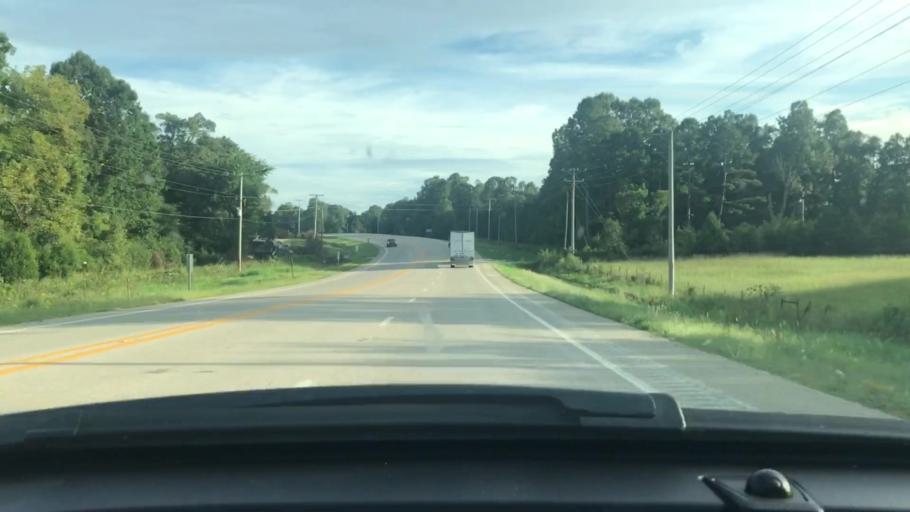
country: US
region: Arkansas
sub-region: Lawrence County
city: Hoxie
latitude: 36.1324
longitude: -91.1583
